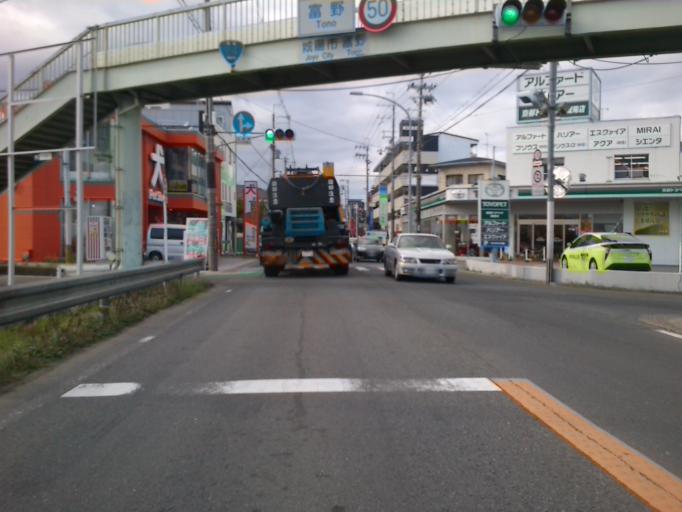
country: JP
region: Kyoto
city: Tanabe
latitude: 34.8387
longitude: 135.7899
